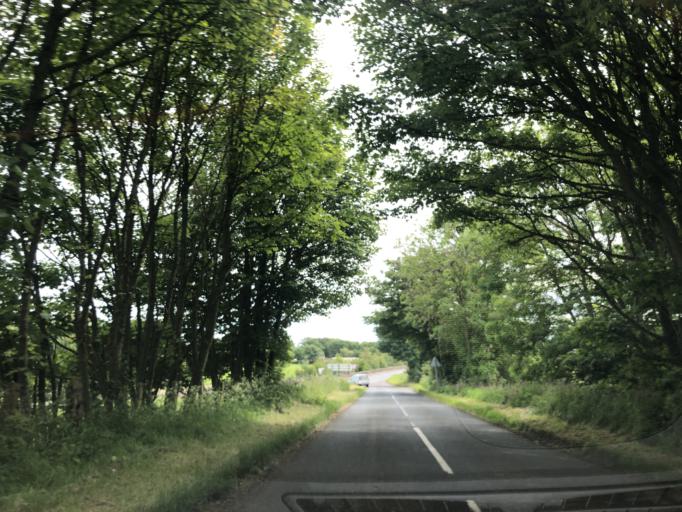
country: GB
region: Scotland
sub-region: Fife
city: Anstruther
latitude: 56.2654
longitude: -2.6352
